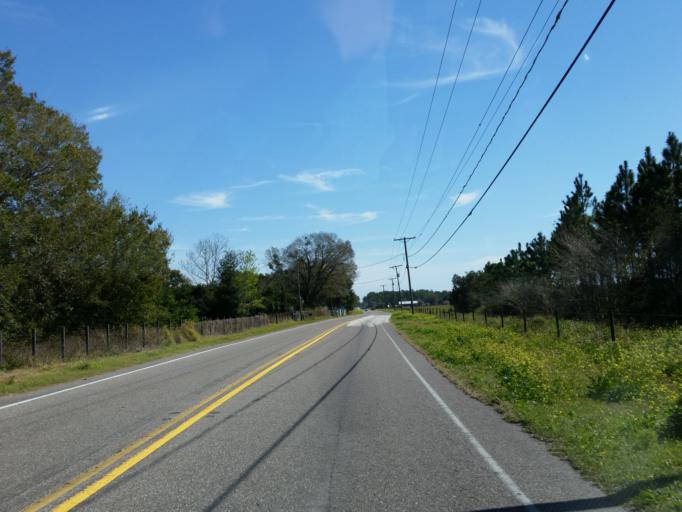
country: US
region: Florida
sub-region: Hillsborough County
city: Balm
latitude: 27.7627
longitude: -82.2225
